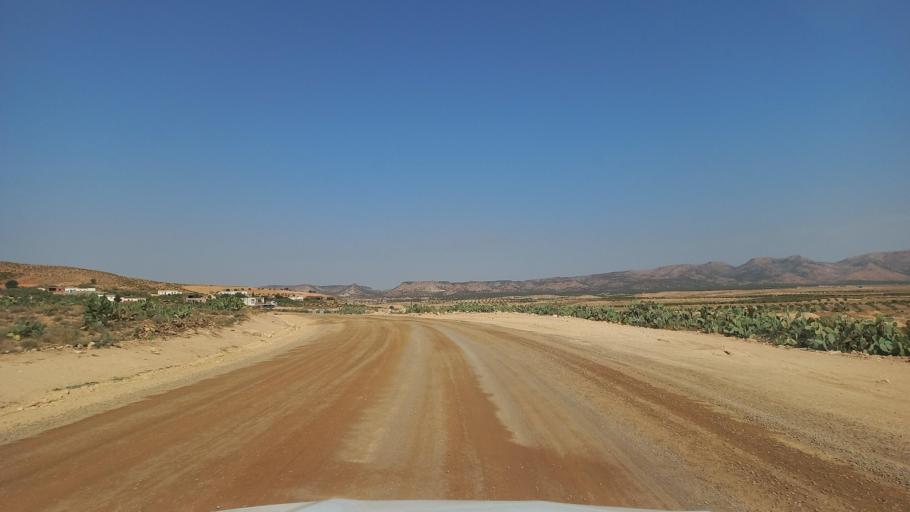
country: TN
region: Al Qasrayn
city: Sbiba
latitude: 35.3828
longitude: 9.0284
